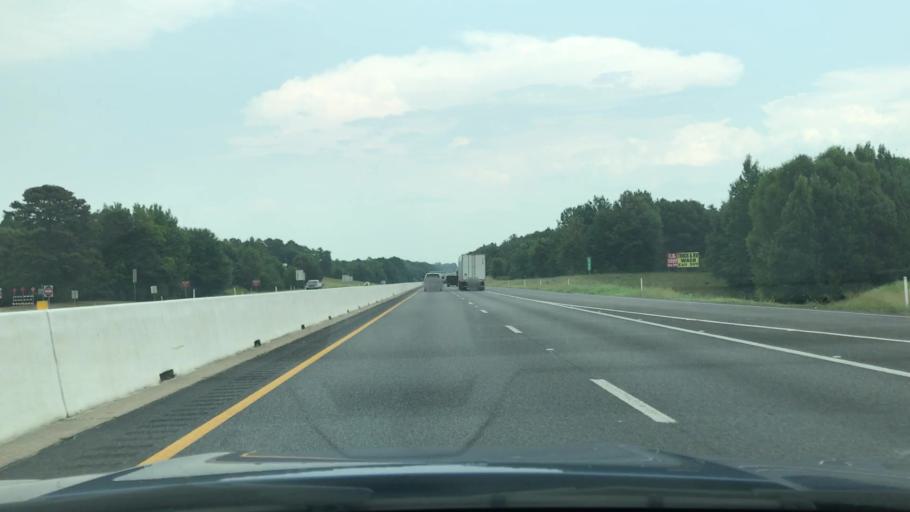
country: US
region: Texas
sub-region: Gregg County
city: Liberty City
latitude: 32.4363
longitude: -94.9863
